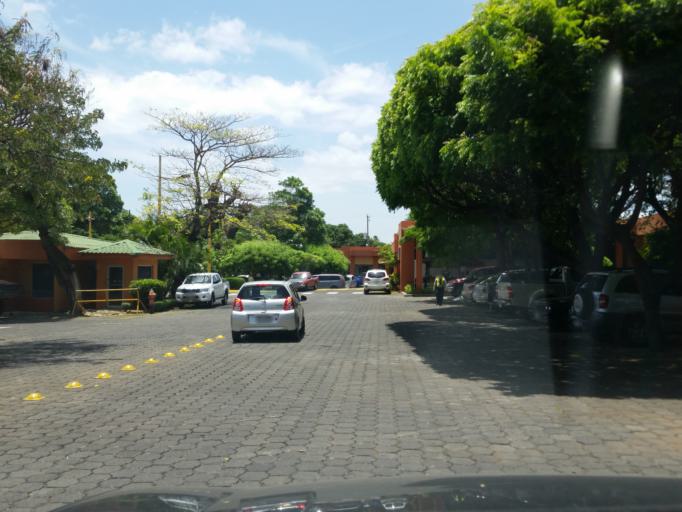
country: NI
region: Managua
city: Managua
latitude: 12.1156
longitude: -86.2477
